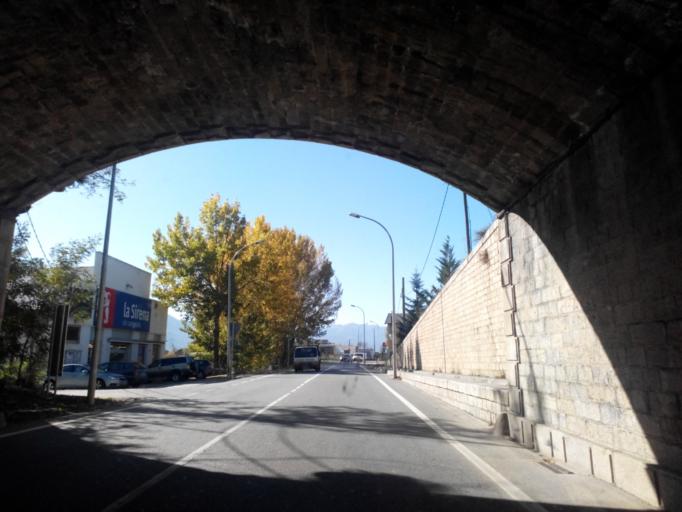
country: ES
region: Catalonia
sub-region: Provincia de Girona
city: Puigcerda
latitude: 42.4268
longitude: 1.9274
